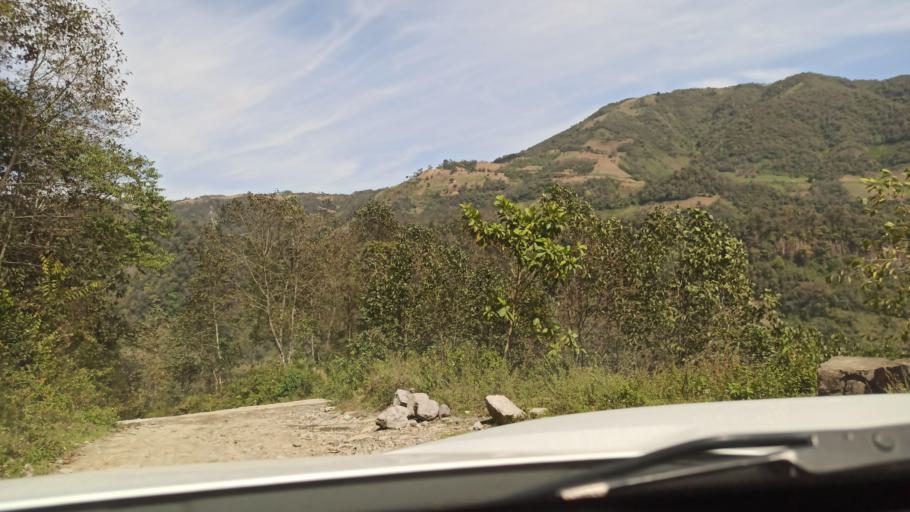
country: MX
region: Veracruz
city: Xocotla
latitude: 18.9816
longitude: -97.0972
